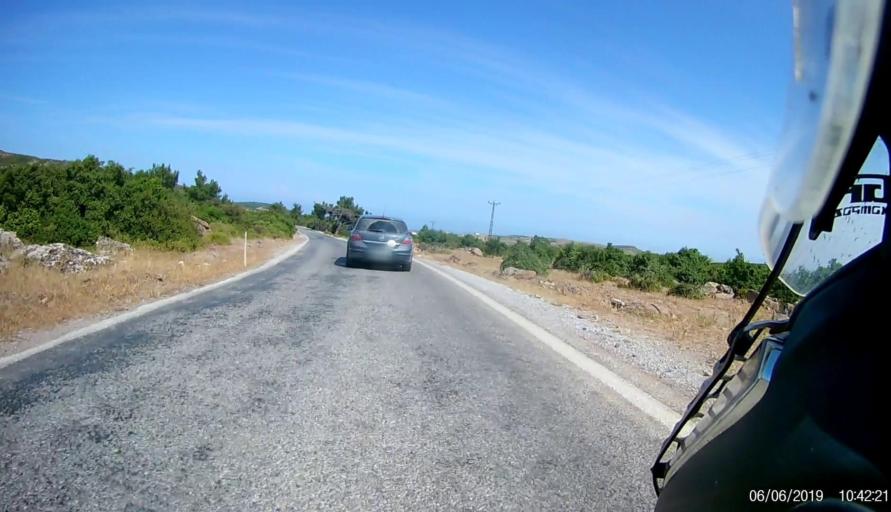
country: TR
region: Canakkale
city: Ayvacik
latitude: 39.5119
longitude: 26.4320
